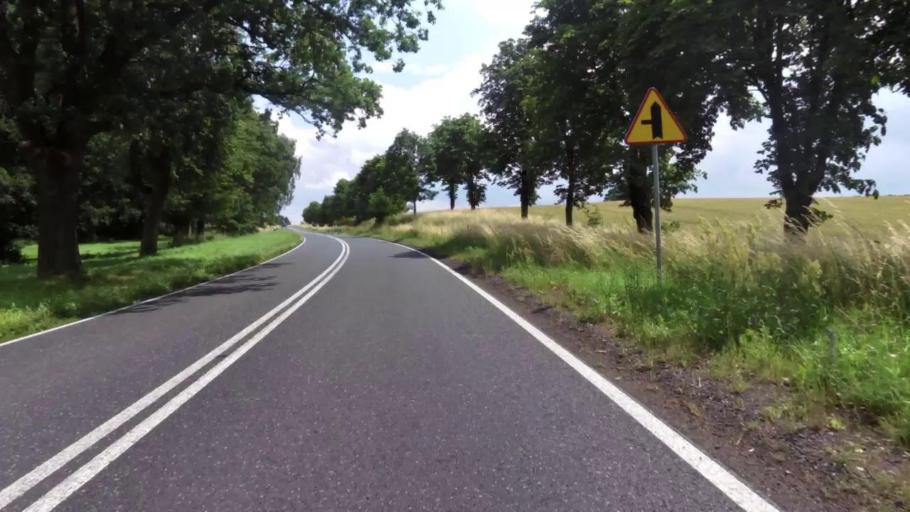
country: PL
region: West Pomeranian Voivodeship
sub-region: Powiat mysliborski
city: Nowogrodek Pomorski
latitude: 52.9942
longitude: 15.0848
